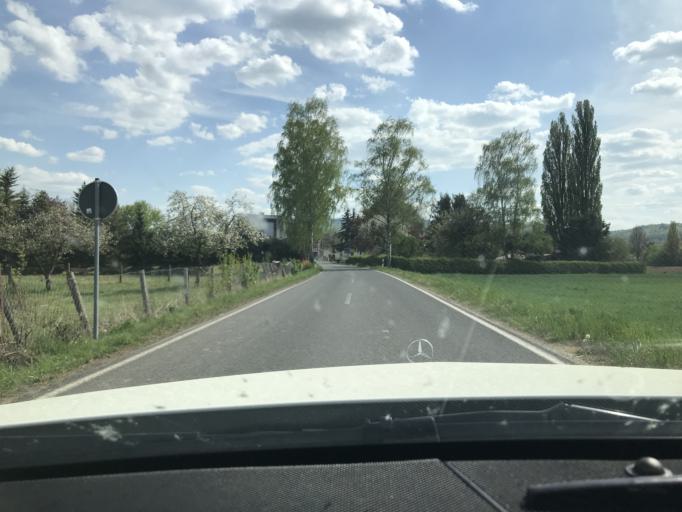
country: DE
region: Hesse
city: Wanfried
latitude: 51.1530
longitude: 10.1772
